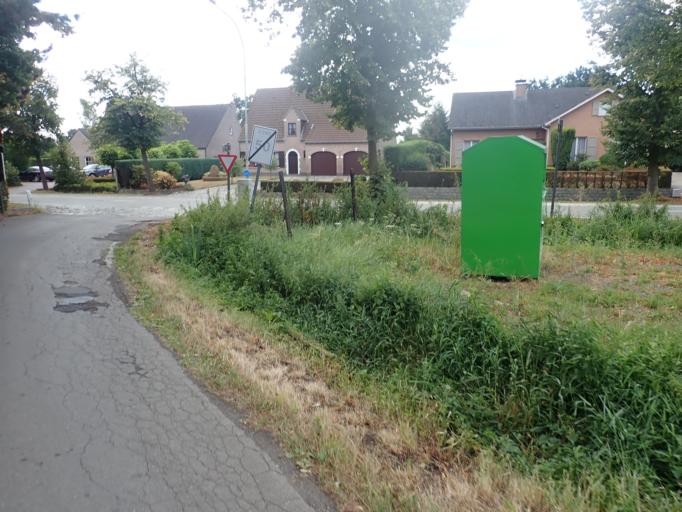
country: BE
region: Flanders
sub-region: Provincie Antwerpen
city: Heist-op-den-Berg
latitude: 51.0694
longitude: 4.7507
